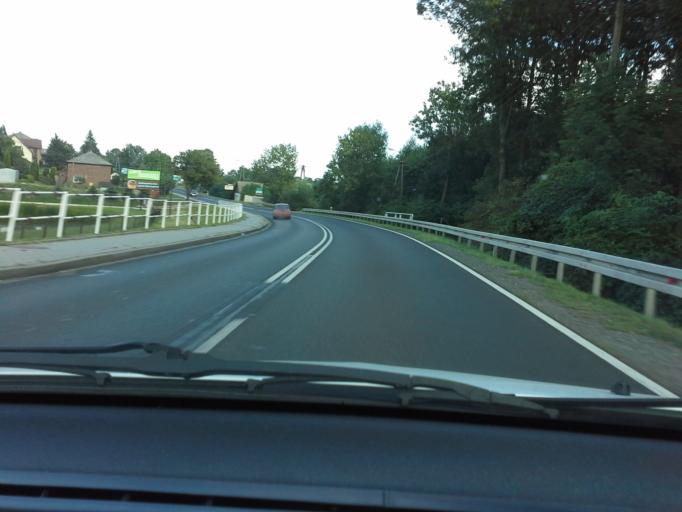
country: PL
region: Lesser Poland Voivodeship
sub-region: Powiat chrzanowski
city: Psary
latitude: 50.1427
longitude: 19.5157
